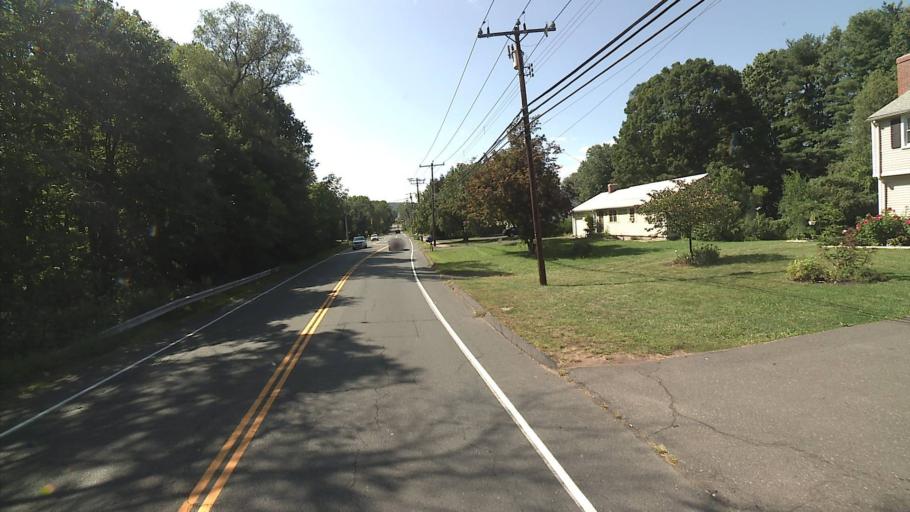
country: US
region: Connecticut
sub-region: Hartford County
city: Blue Hills
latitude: 41.8303
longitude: -72.7474
